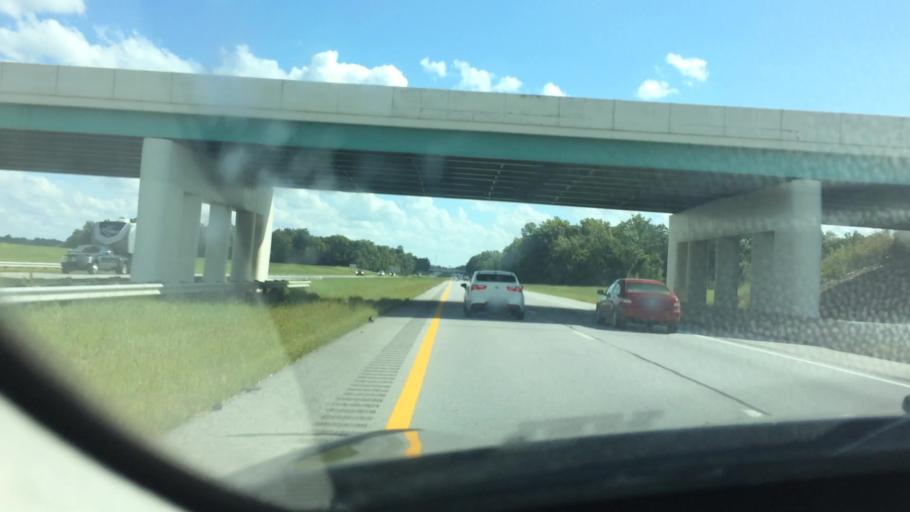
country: US
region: Ohio
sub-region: Shelby County
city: Botkins
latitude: 40.4397
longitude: -84.1698
